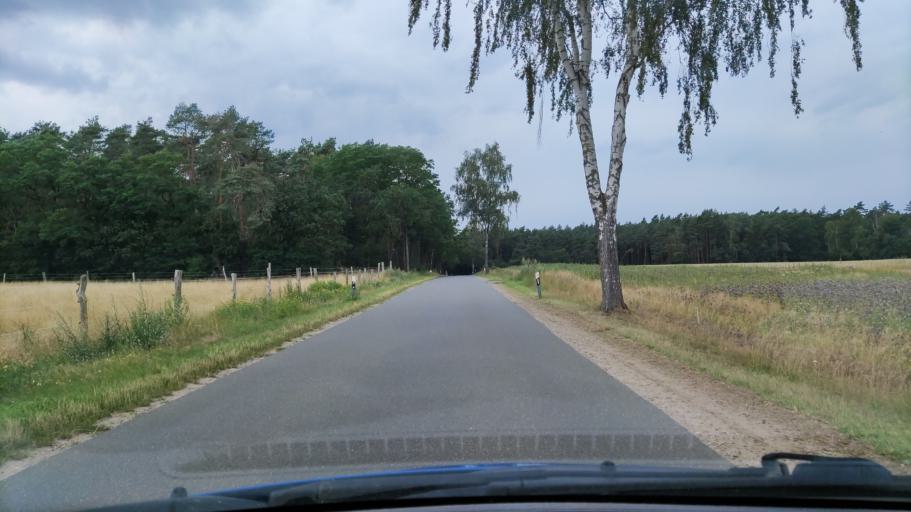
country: DE
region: Lower Saxony
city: Suhlendorf
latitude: 52.9678
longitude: 10.8256
